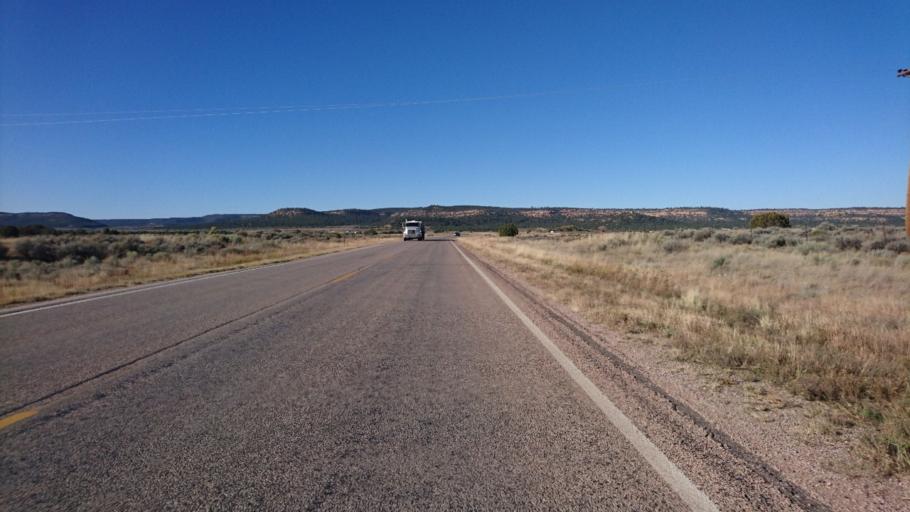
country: US
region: New Mexico
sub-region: McKinley County
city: Black Rock
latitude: 35.1069
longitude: -108.5671
